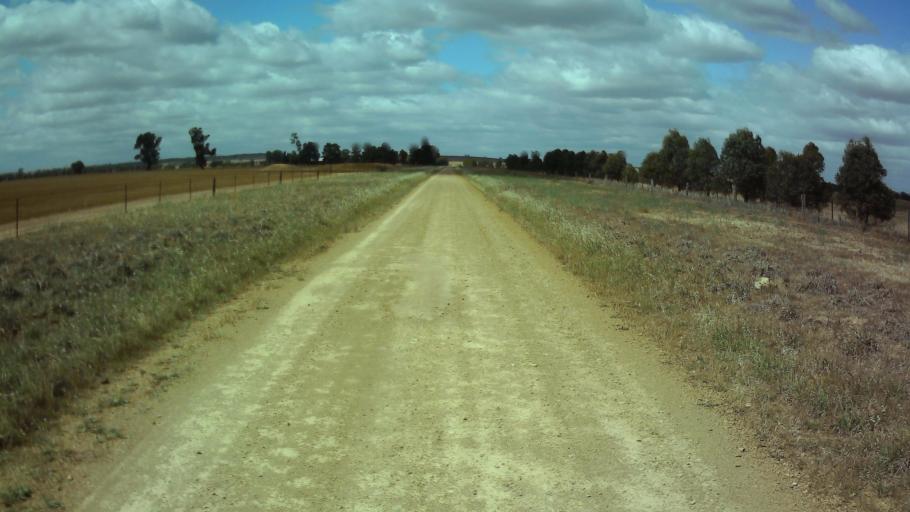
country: AU
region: New South Wales
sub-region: Weddin
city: Grenfell
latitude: -34.0546
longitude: 148.3314
